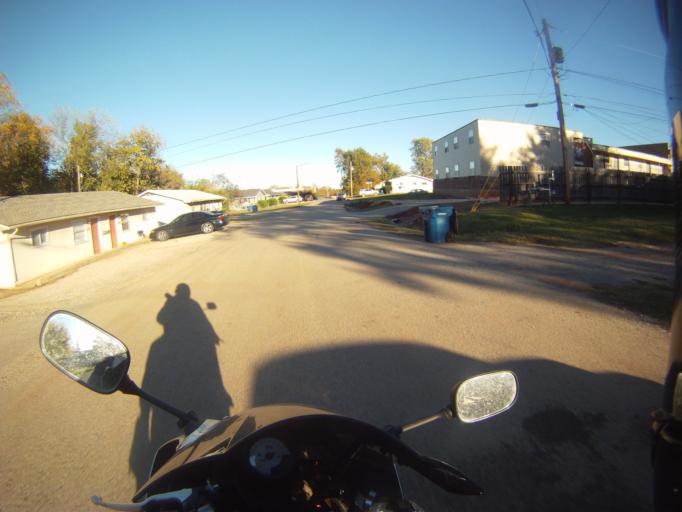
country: US
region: Oklahoma
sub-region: Payne County
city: Stillwater
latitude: 36.1316
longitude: -97.0721
